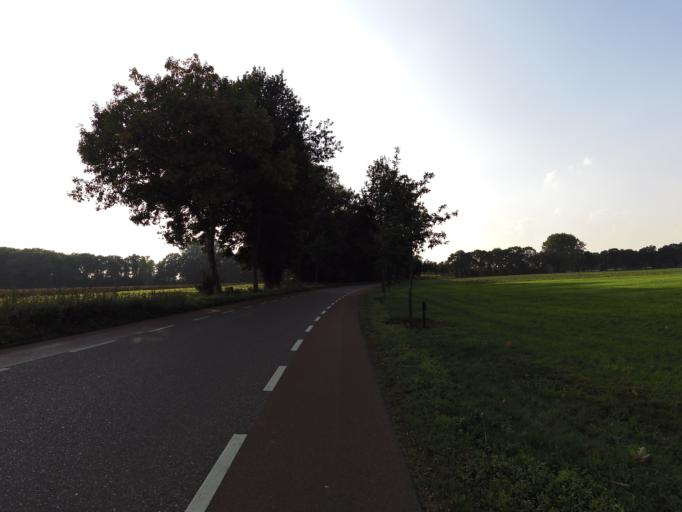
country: NL
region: Gelderland
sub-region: Gemeente Aalten
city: Aalten
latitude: 51.9187
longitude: 6.5521
